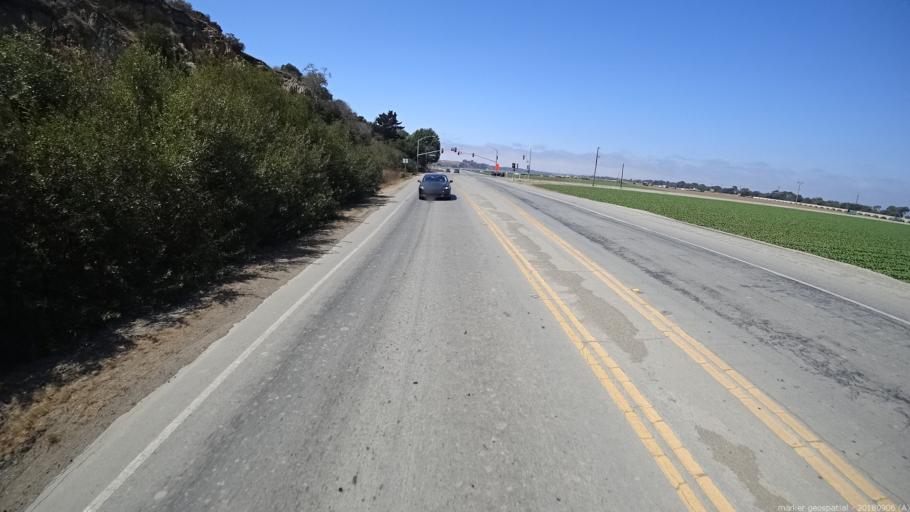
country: US
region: California
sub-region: Monterey County
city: Salinas
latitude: 36.6413
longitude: -121.7057
